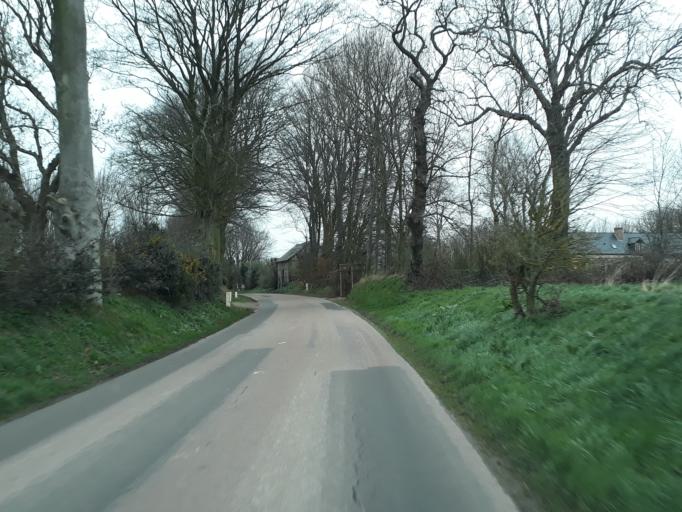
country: FR
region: Haute-Normandie
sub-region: Departement de la Seine-Maritime
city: Les Loges
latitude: 49.7203
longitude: 0.2823
